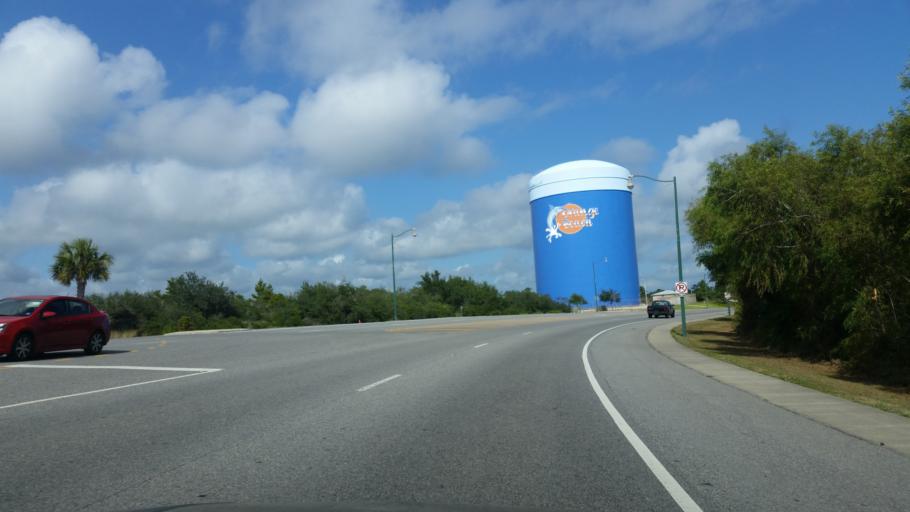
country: US
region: Alabama
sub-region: Baldwin County
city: Orange Beach
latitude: 30.2716
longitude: -87.5857
